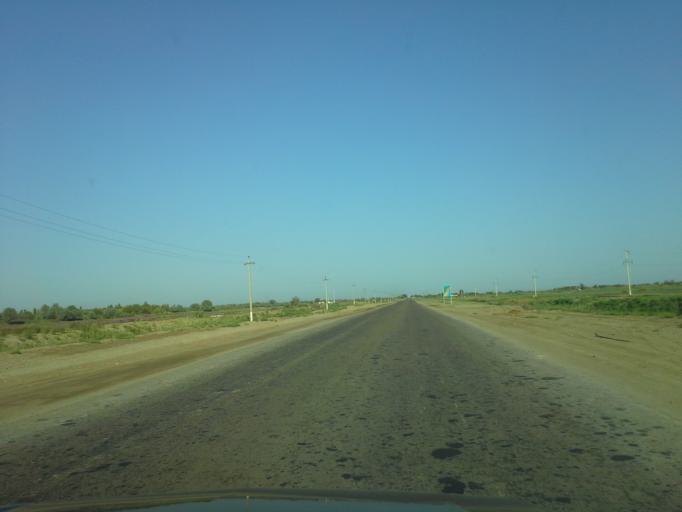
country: UZ
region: Karakalpakstan
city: Khujayli
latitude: 42.2231
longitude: 59.4834
